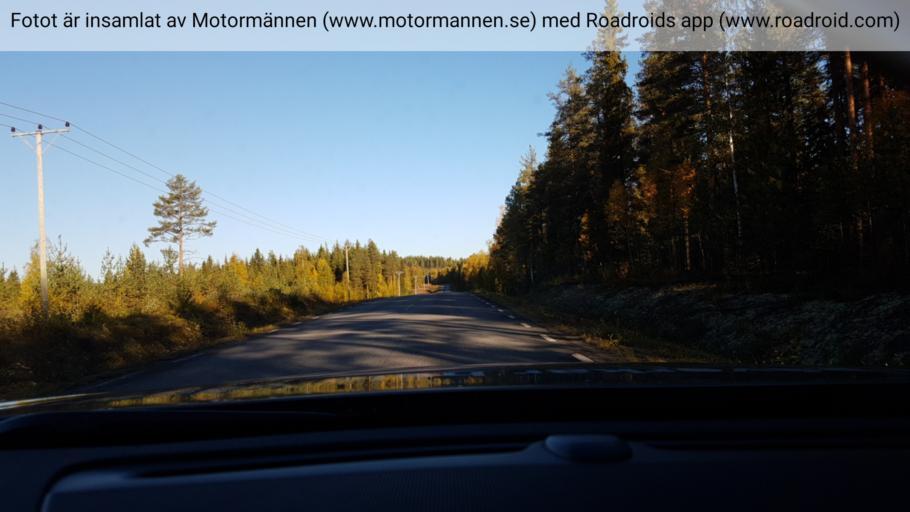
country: SE
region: Norrbotten
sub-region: Bodens Kommun
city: Boden
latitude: 65.9425
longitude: 21.6369
